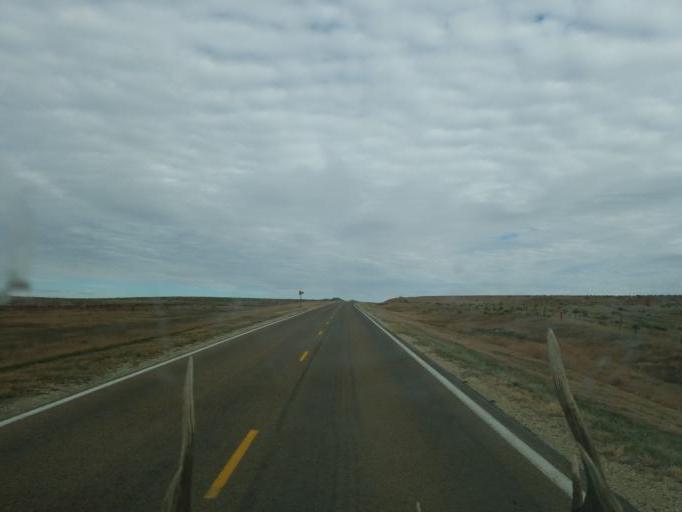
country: US
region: Kansas
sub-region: Wallace County
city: Sharon Springs
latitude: 39.0197
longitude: -101.3436
